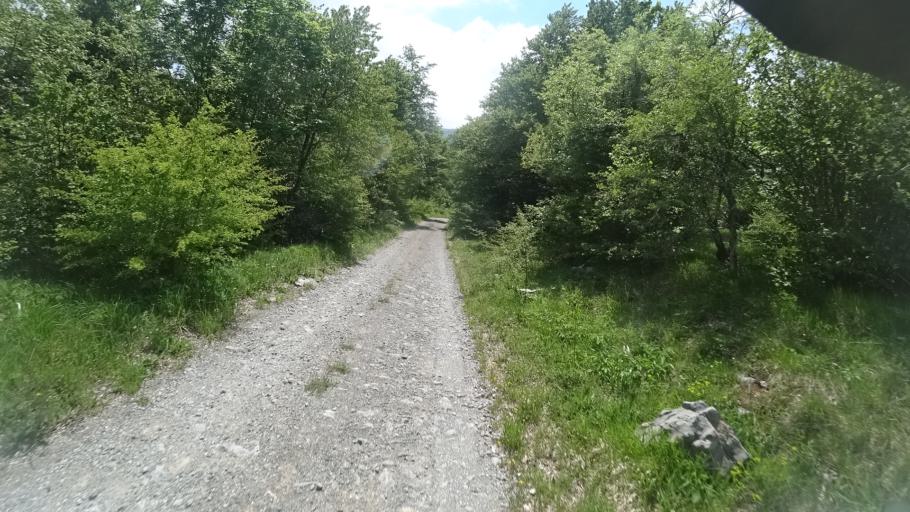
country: HR
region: Zadarska
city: Gracac
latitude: 44.4971
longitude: 15.8786
